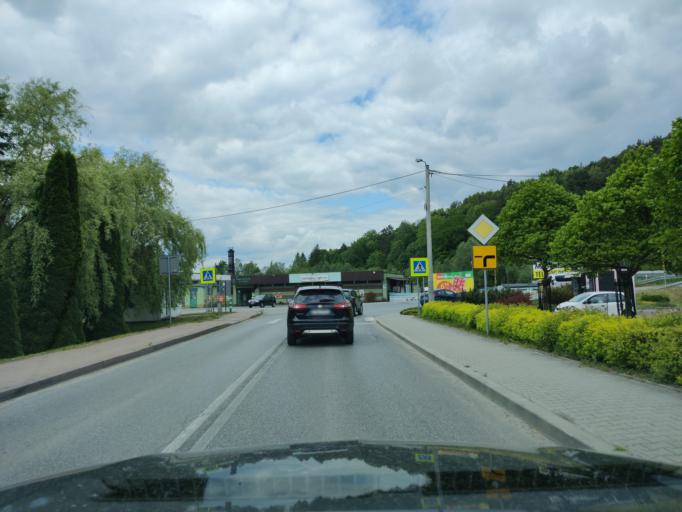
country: PL
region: Lesser Poland Voivodeship
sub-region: Powiat myslenicki
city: Sulkowice
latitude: 49.8559
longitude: 19.7987
